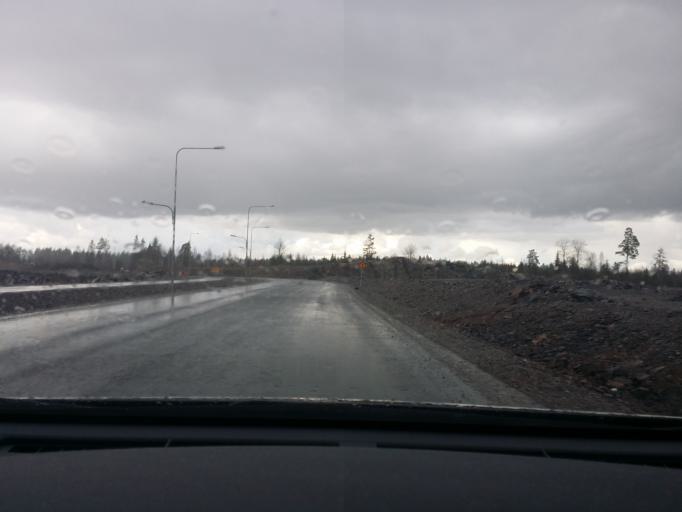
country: SE
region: Soedermanland
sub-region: Eskilstuna Kommun
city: Arla
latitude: 59.3637
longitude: 16.6999
